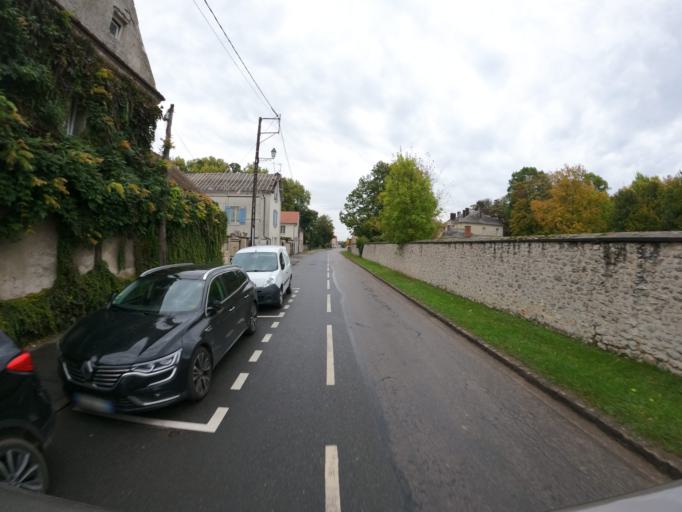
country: FR
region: Ile-de-France
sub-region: Departement de Seine-et-Marne
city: Chanteloup-en-Brie
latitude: 48.8365
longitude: 2.7530
